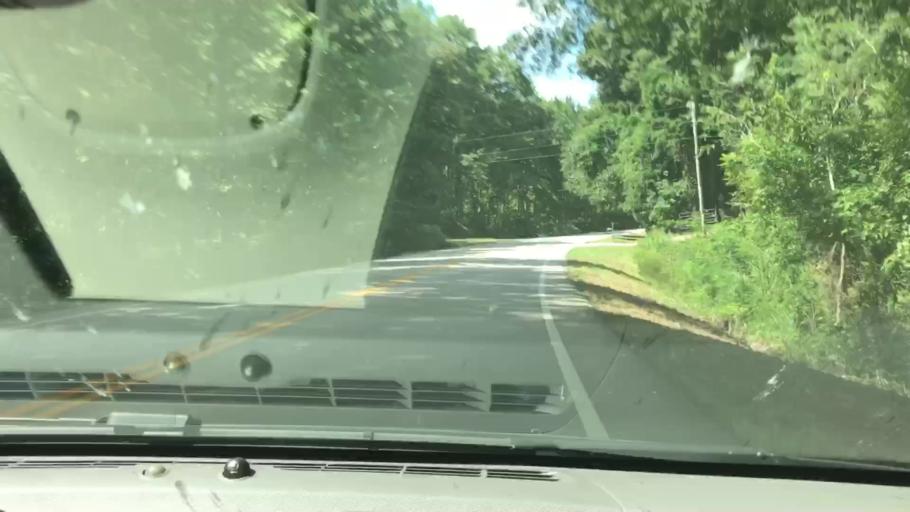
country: US
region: Georgia
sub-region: Troup County
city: La Grange
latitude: 33.1162
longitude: -85.0877
